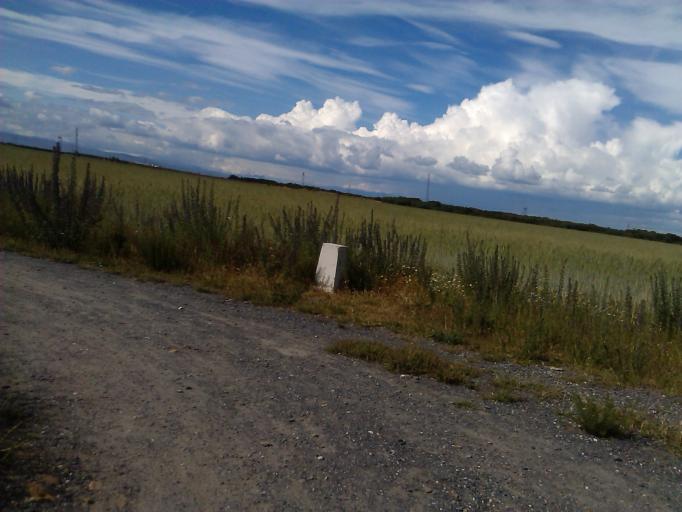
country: ES
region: Castille and Leon
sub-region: Provincia de Leon
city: San Justo de la Vega
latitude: 42.4496
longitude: -5.9830
